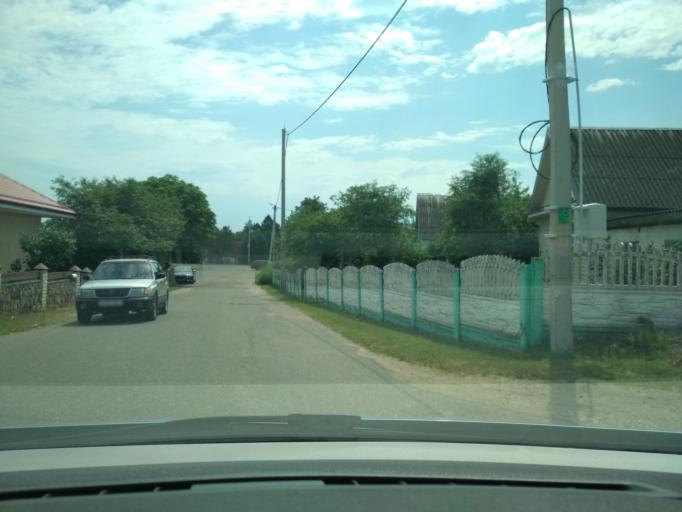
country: BY
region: Grodnenskaya
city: Astravyets
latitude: 54.6147
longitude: 25.9509
